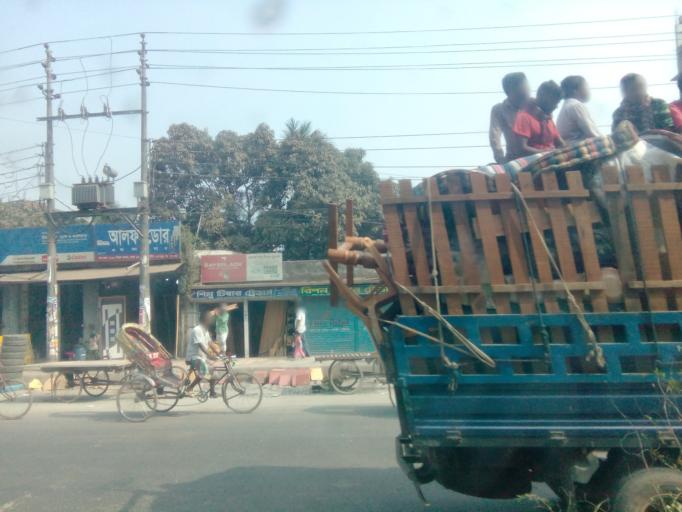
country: BD
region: Dhaka
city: Paltan
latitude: 23.7843
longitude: 90.4260
